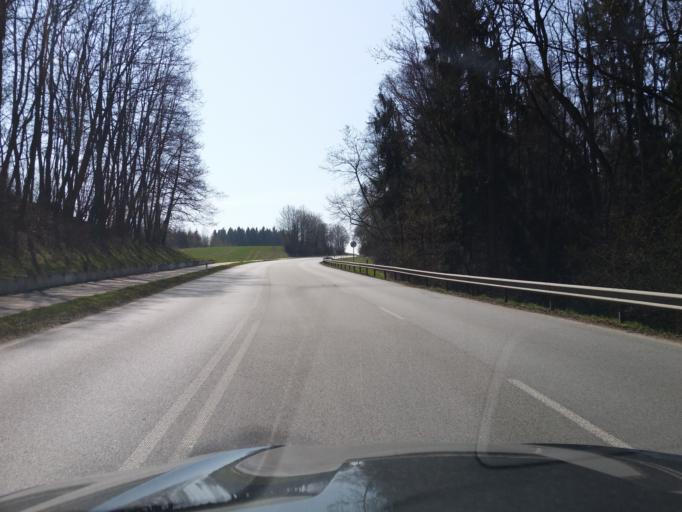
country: DE
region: Bavaria
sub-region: Lower Bavaria
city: Kumhausen
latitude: 48.4788
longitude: 12.1576
